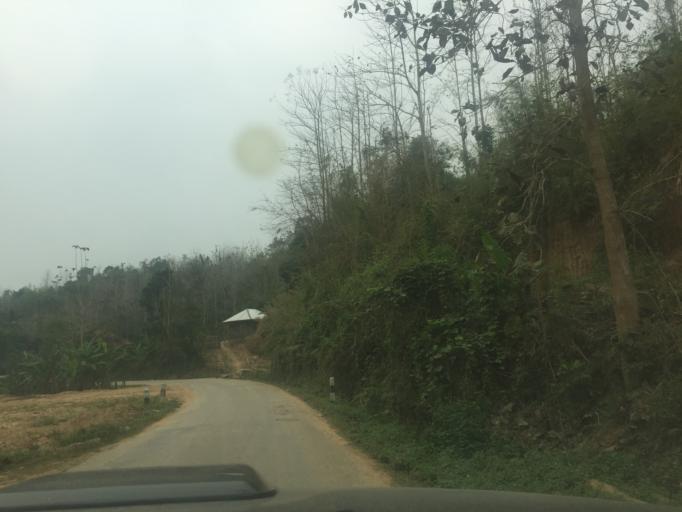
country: LA
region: Vientiane
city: Muang Sanakham
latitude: 18.3919
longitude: 101.5187
